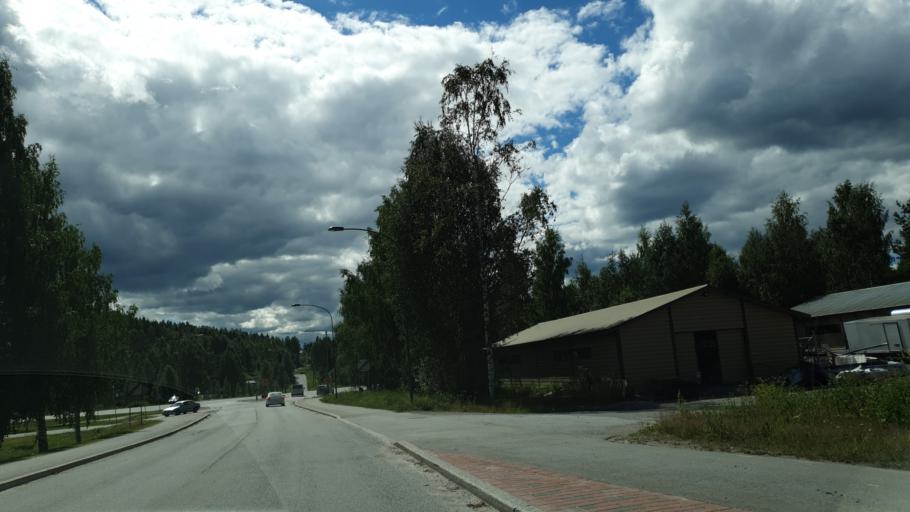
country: FI
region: North Karelia
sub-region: Pielisen Karjala
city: Nurmes
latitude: 63.5537
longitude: 29.0982
